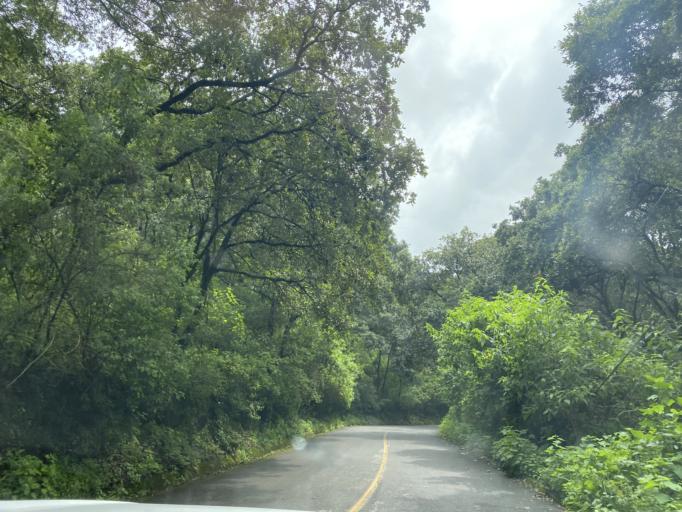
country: MX
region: Morelos
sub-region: Yecapixtla
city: Achichipico
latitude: 18.9396
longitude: -98.8210
